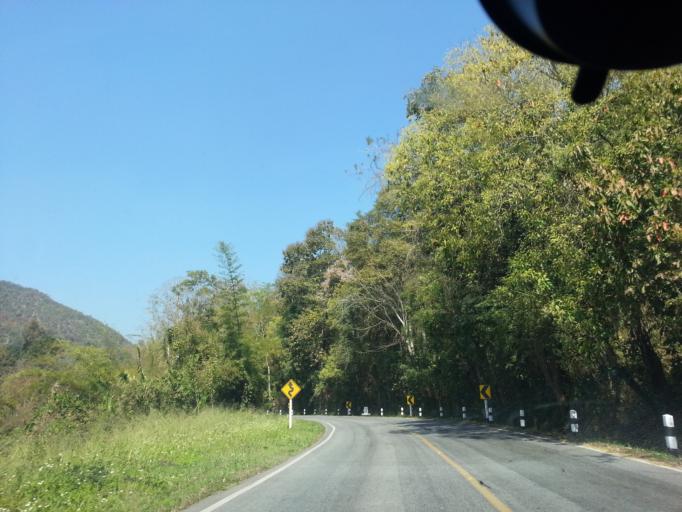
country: TH
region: Chiang Mai
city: Chai Prakan
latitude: 19.5659
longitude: 99.0787
